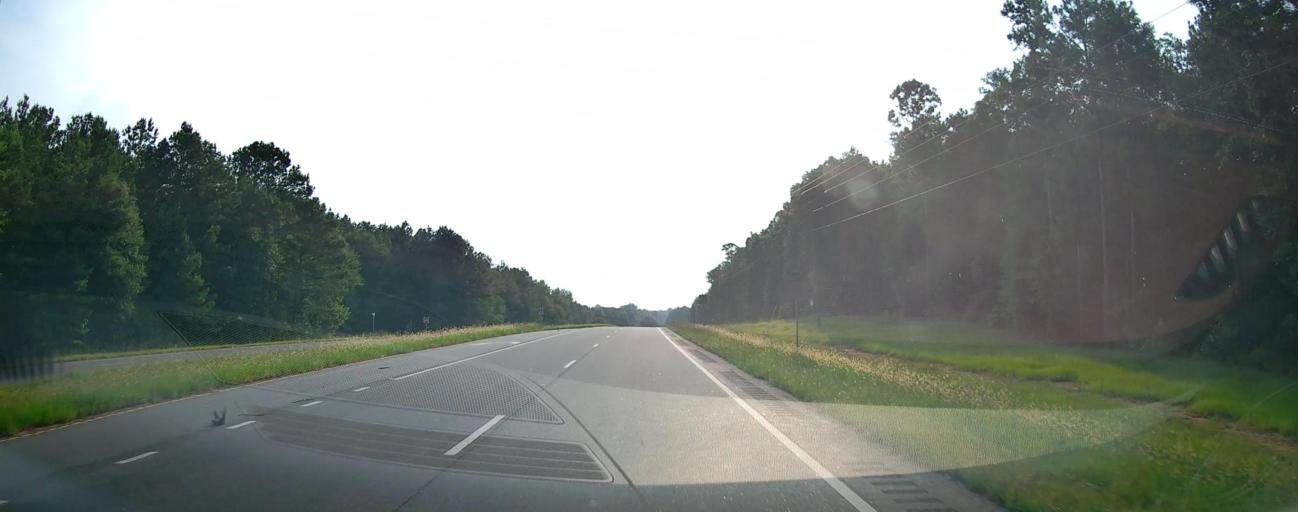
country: US
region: Georgia
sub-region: Talbot County
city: Talbotton
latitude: 32.5459
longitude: -84.7207
